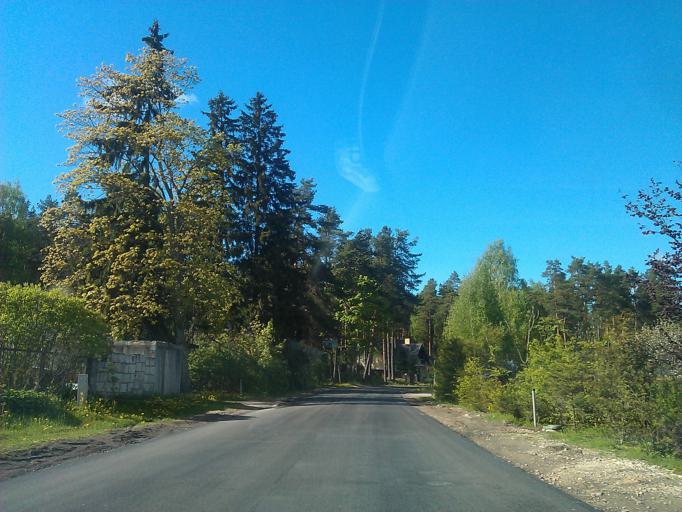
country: LV
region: Riga
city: Bergi
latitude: 57.0143
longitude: 24.2595
